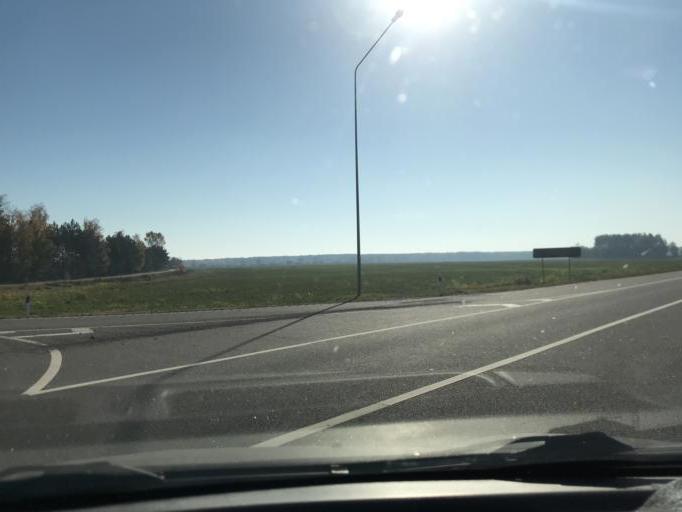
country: BY
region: Mogilev
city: Babruysk
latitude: 53.1285
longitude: 29.3647
